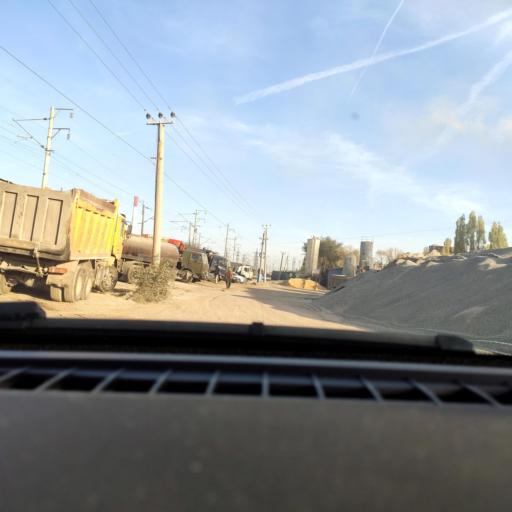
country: RU
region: Voronezj
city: Maslovka
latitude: 51.6249
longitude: 39.2576
